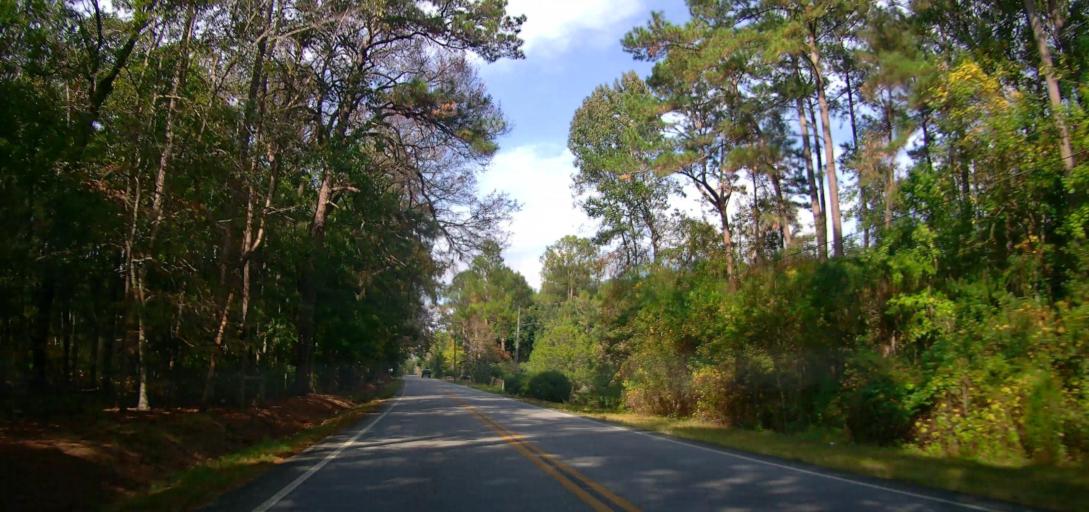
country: US
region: Georgia
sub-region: Thomas County
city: Thomasville
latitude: 30.8883
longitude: -84.0063
